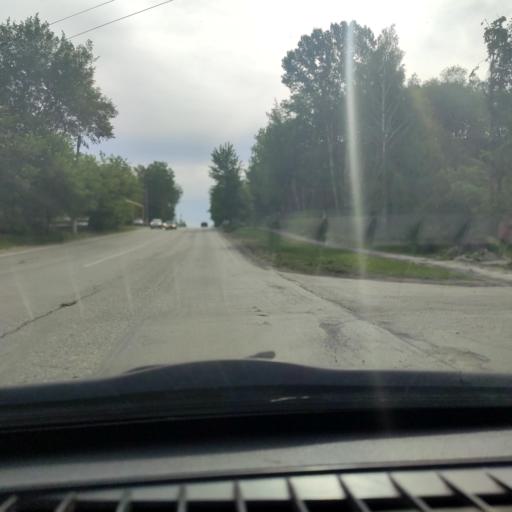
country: RU
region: Samara
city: Zhigulevsk
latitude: 53.4035
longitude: 49.5042
